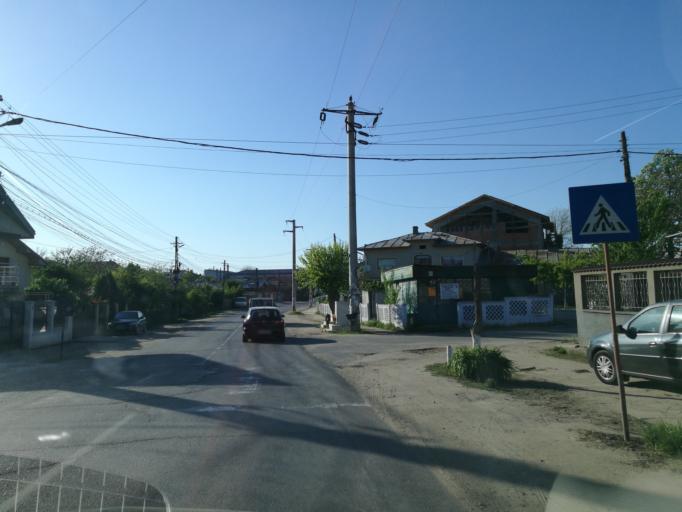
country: RO
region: Ilfov
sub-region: Comuna Berceni
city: Berceni
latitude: 44.3151
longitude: 26.1860
